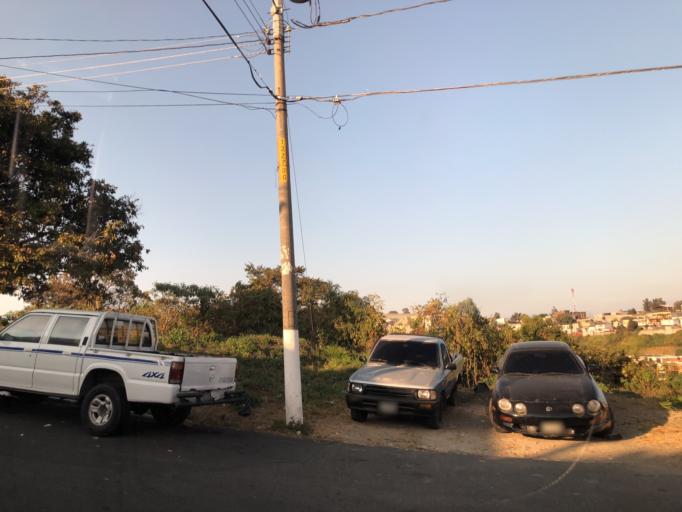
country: GT
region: Guatemala
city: Mixco
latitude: 14.6276
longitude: -90.5928
